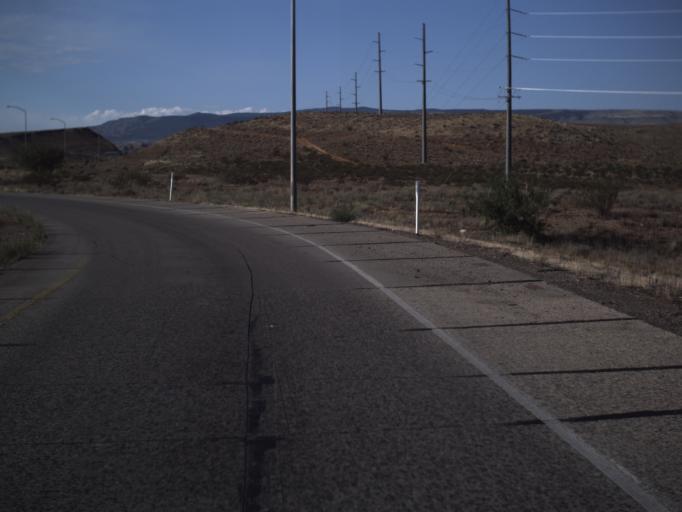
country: US
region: Utah
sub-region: Washington County
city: Saint George
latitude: 37.0113
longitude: -113.6167
